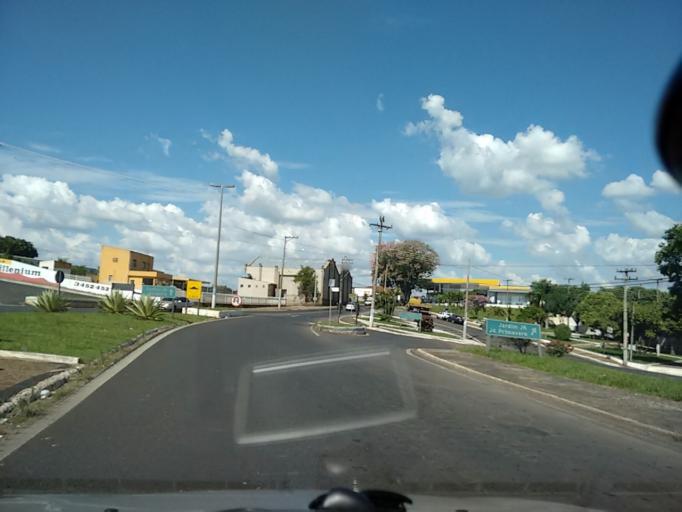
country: BR
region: Sao Paulo
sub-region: Pompeia
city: Pompeia
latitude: -22.1032
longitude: -50.1885
